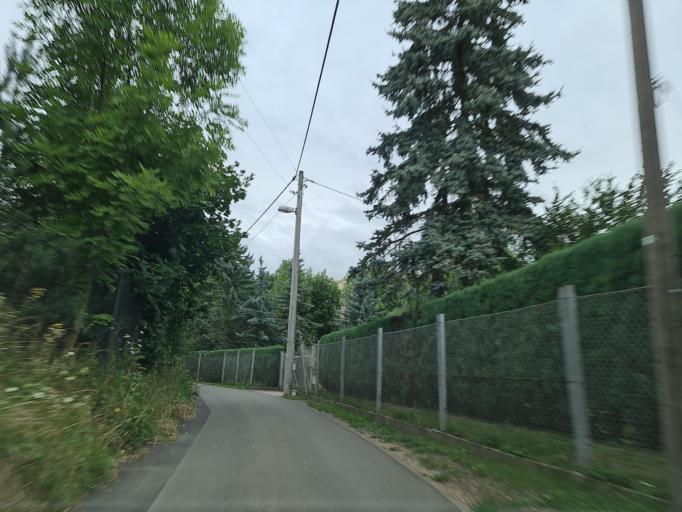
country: DE
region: Saxony
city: Plauen
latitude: 50.4990
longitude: 12.1012
